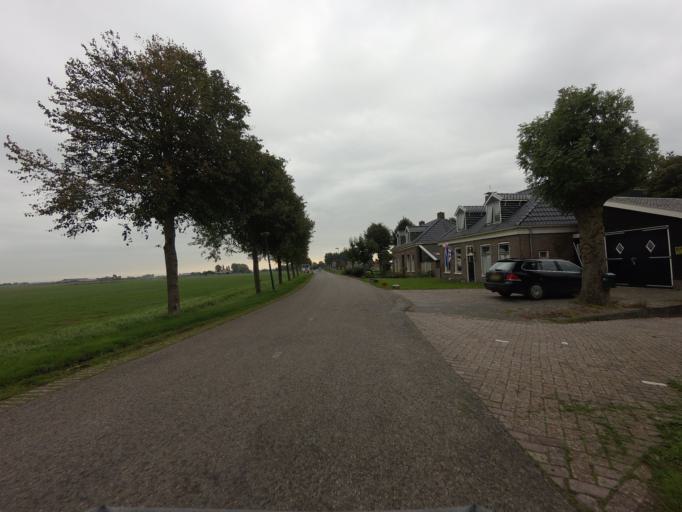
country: NL
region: Friesland
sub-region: Sudwest Fryslan
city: Bolsward
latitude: 53.0208
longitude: 5.5361
